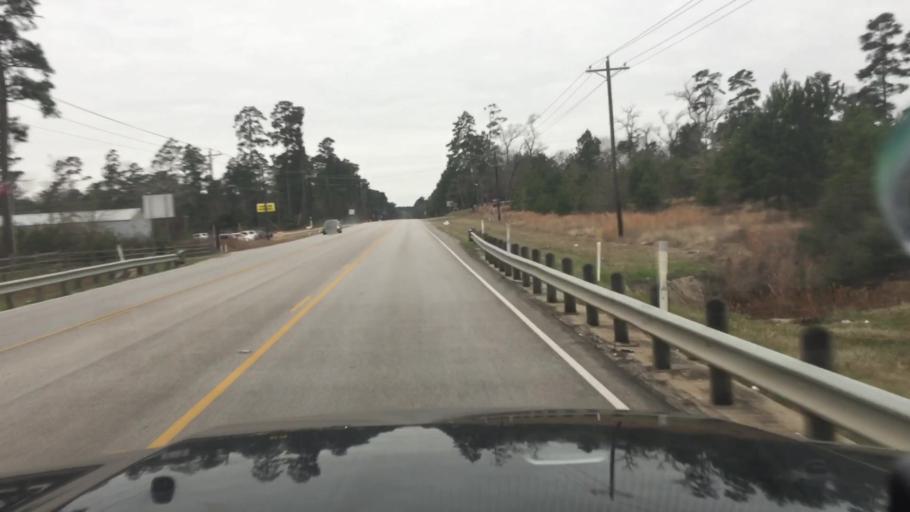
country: US
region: Texas
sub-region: Montgomery County
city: Magnolia
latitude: 30.1896
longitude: -95.8108
